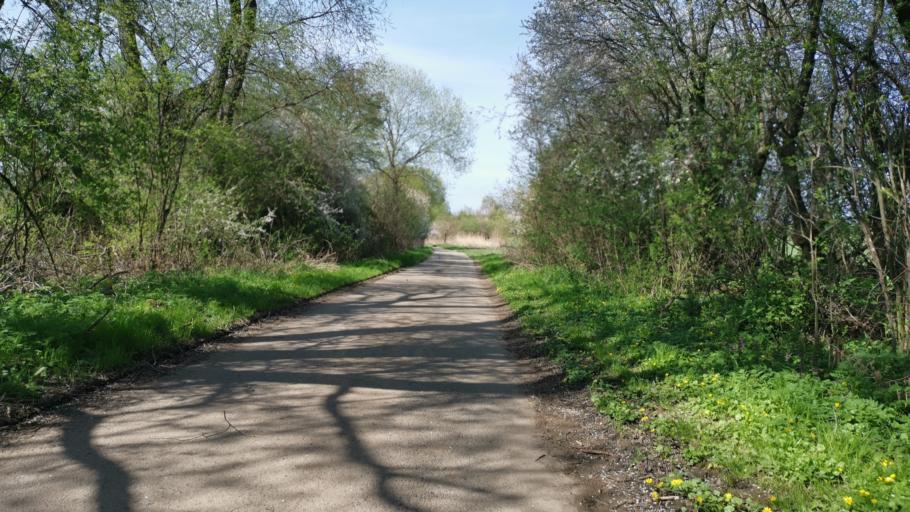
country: SK
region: Trnavsky
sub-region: Okres Skalica
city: Holic
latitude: 48.7632
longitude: 17.1903
